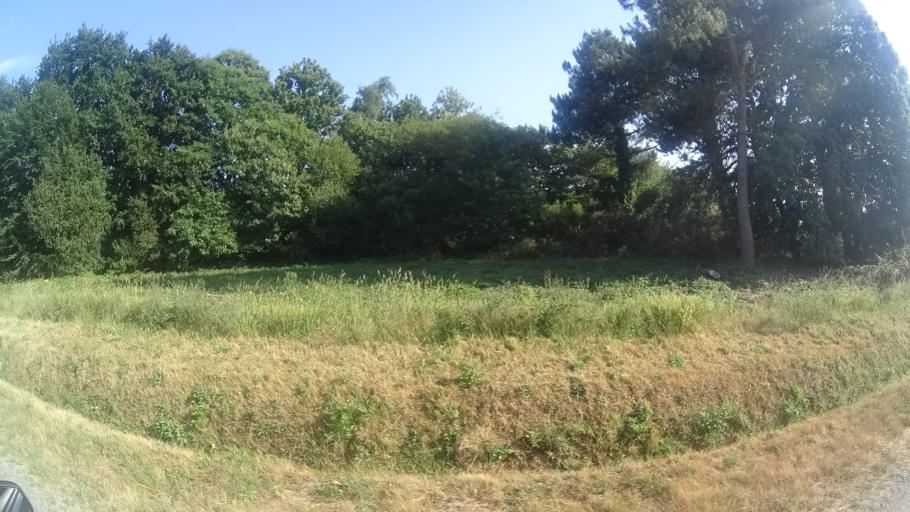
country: FR
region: Brittany
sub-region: Departement du Morbihan
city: Beganne
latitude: 47.5924
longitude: -2.2801
